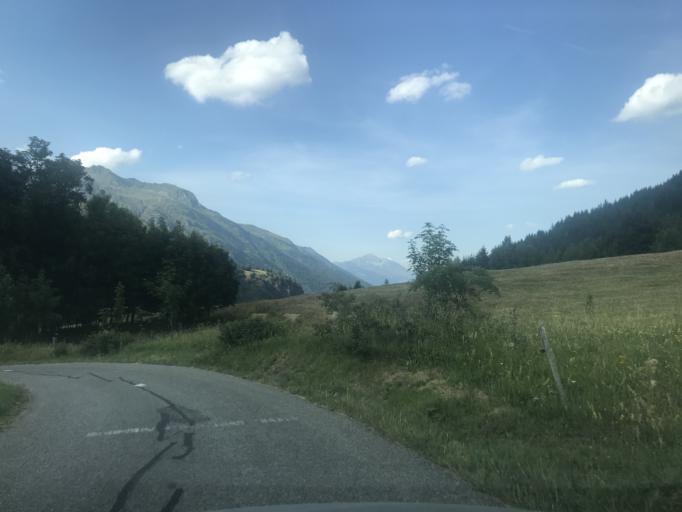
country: FR
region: Rhone-Alpes
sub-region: Departement de la Savoie
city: Saint-Etienne-de-Cuines
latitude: 45.2620
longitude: 6.1966
